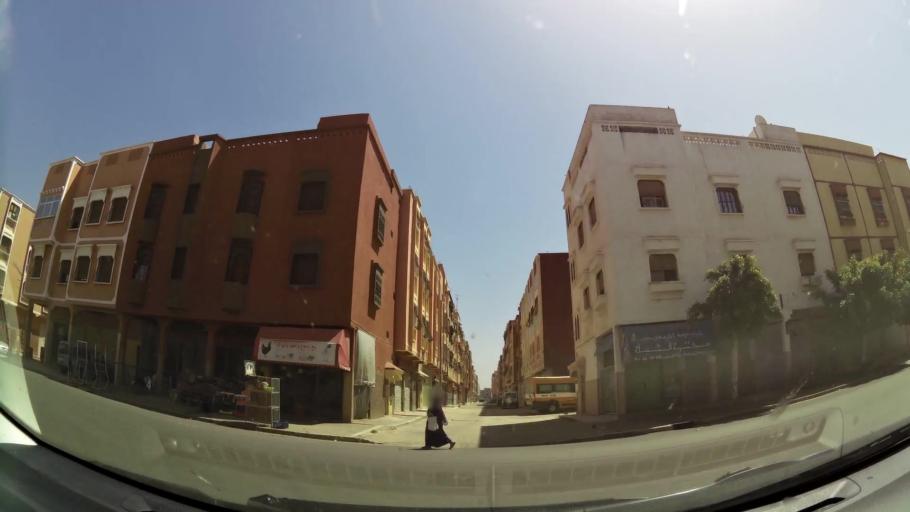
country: MA
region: Souss-Massa-Draa
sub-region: Inezgane-Ait Mellou
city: Inezgane
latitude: 30.3370
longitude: -9.5021
